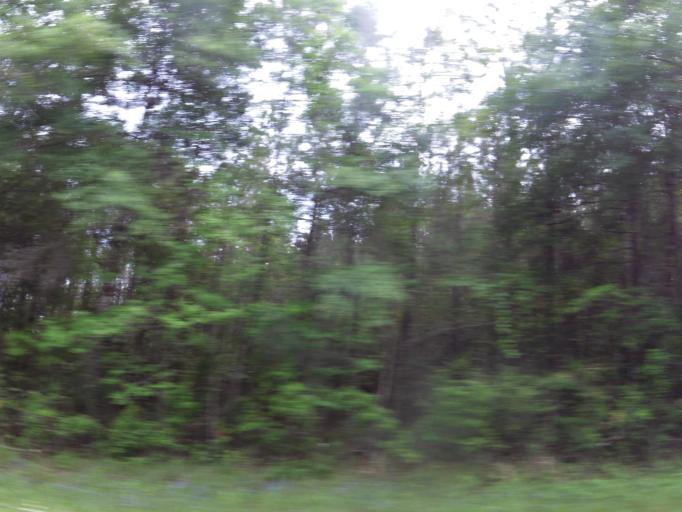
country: US
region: Florida
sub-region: Nassau County
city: Hilliard
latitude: 30.6982
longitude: -81.8935
